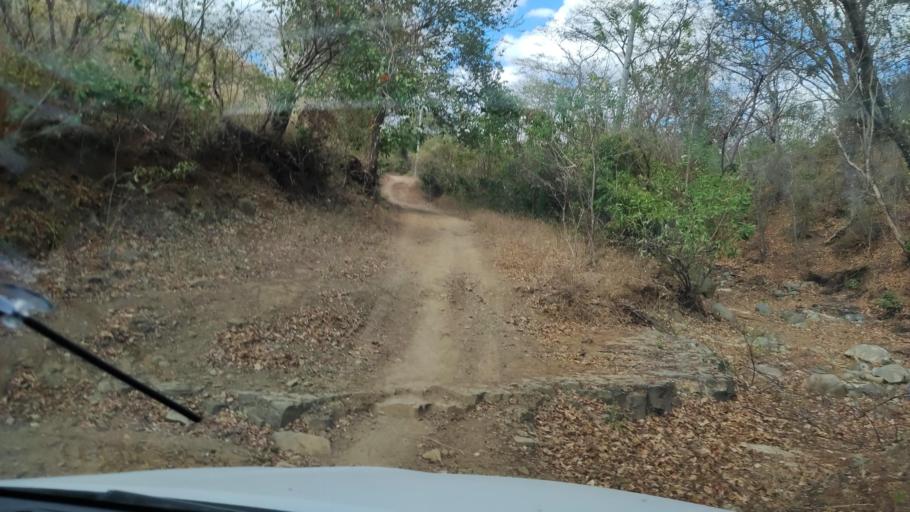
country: NI
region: Carazo
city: Santa Teresa
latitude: 11.6438
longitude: -86.2165
